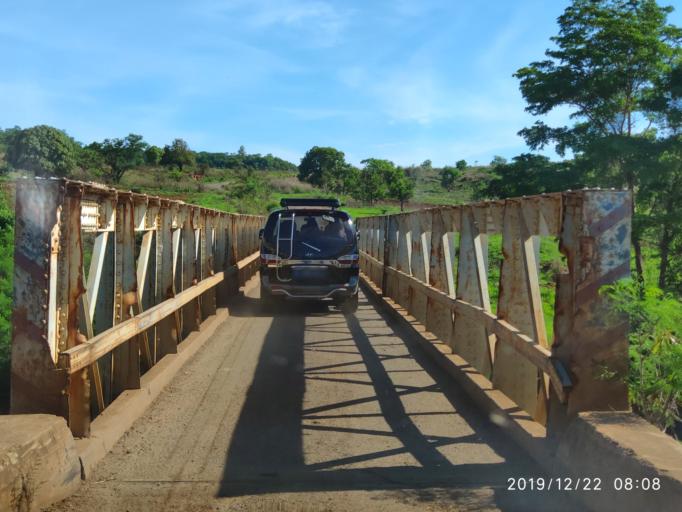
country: MG
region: Diana
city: Ambilobe
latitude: -12.9277
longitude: 49.1630
